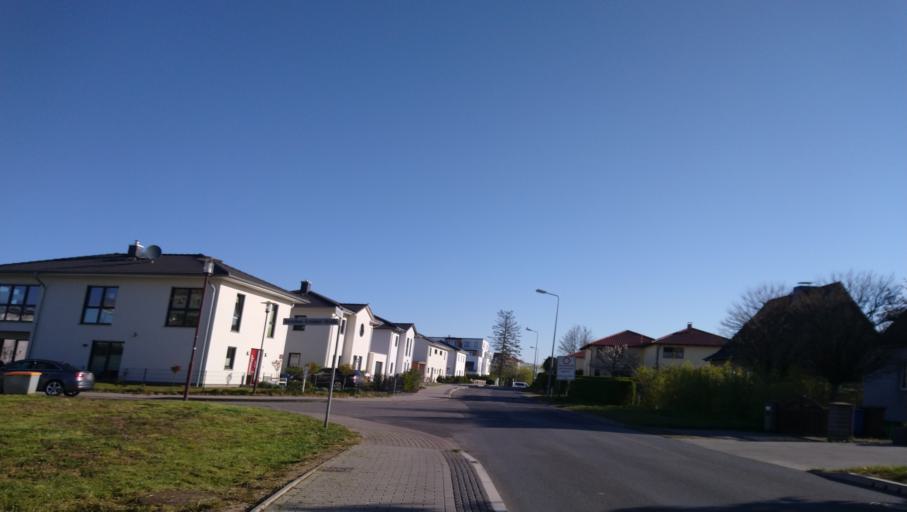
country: DE
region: Mecklenburg-Vorpommern
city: Rostock
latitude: 54.0634
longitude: 12.1299
